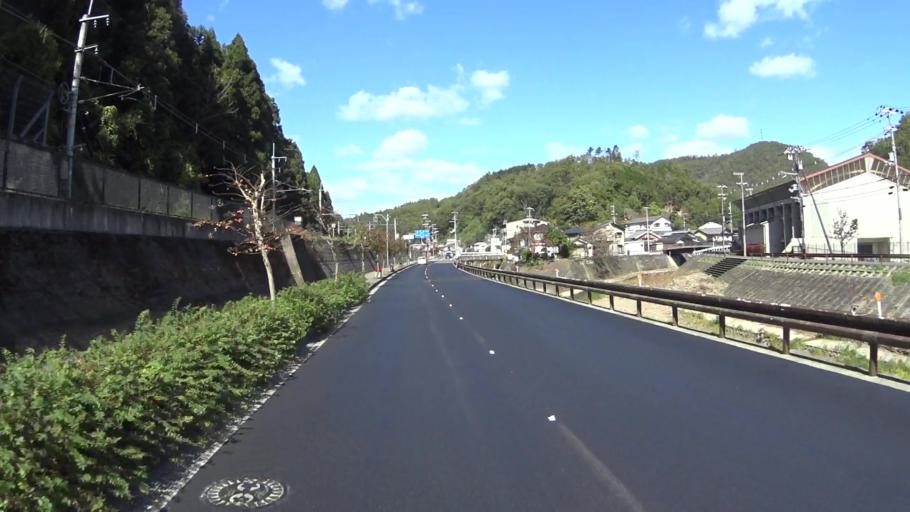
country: JP
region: Kyoto
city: Kameoka
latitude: 35.1595
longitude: 135.5055
